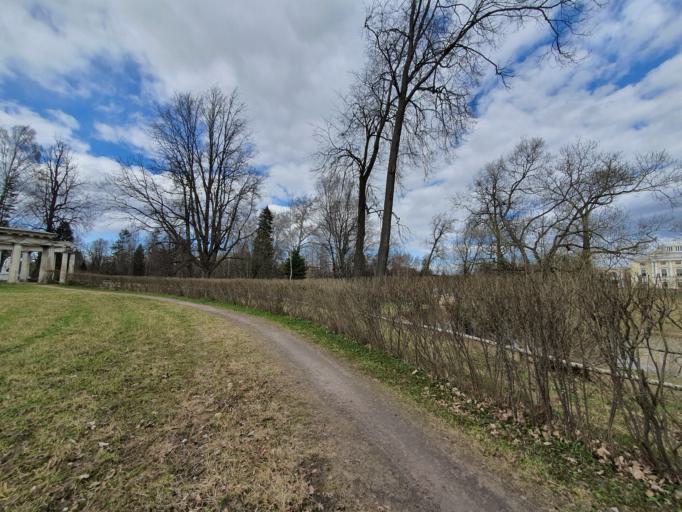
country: RU
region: St.-Petersburg
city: Pavlovsk
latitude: 59.6853
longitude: 30.4485
